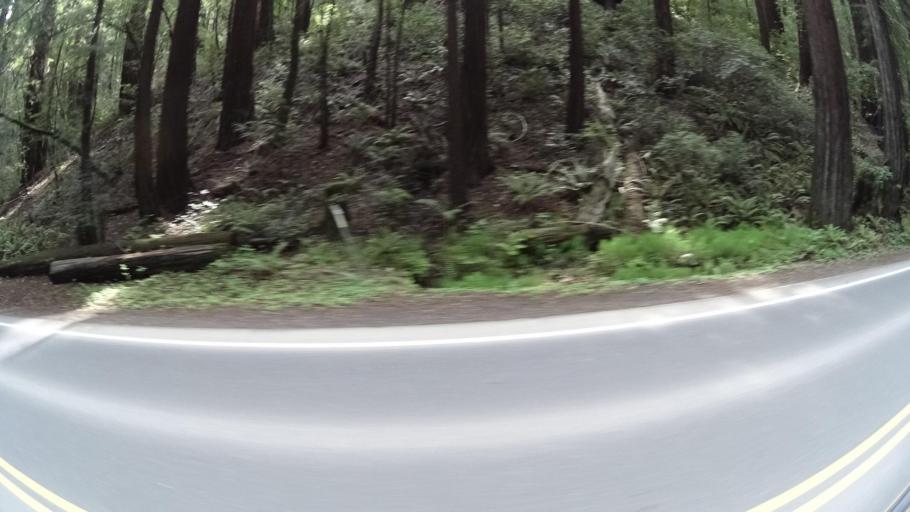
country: US
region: California
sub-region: Humboldt County
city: Redway
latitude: 40.1328
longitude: -123.8171
